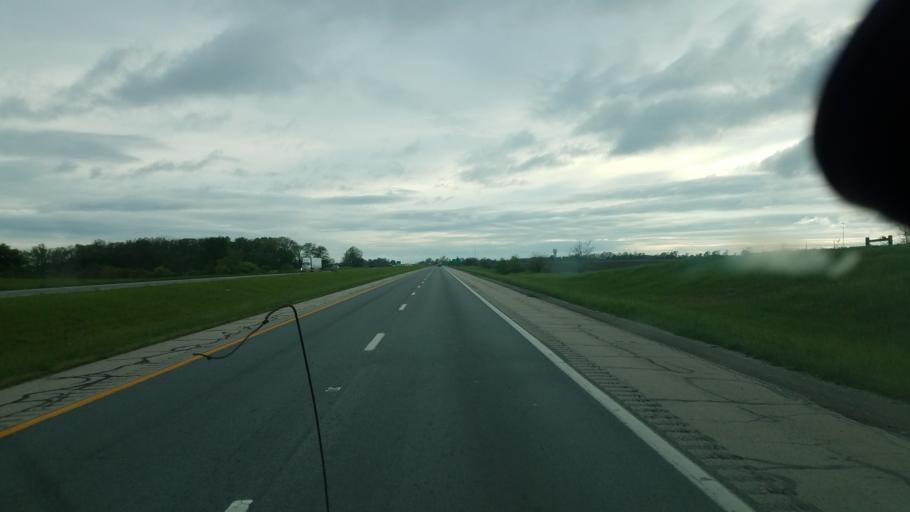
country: US
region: Ohio
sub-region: Madison County
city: Bethel
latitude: 39.7062
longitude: -83.4343
